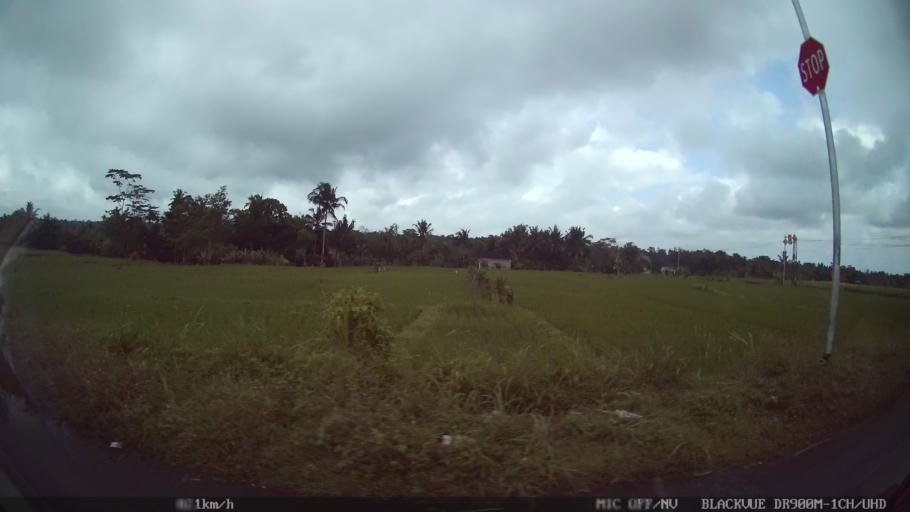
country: ID
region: Bali
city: Banjar Teguan
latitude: -8.5036
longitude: 115.2253
